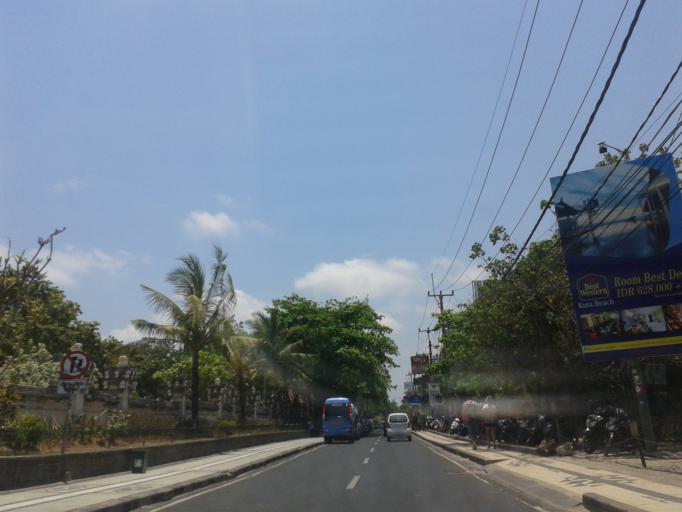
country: ID
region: Bali
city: Kuta
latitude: -8.7139
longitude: 115.1680
